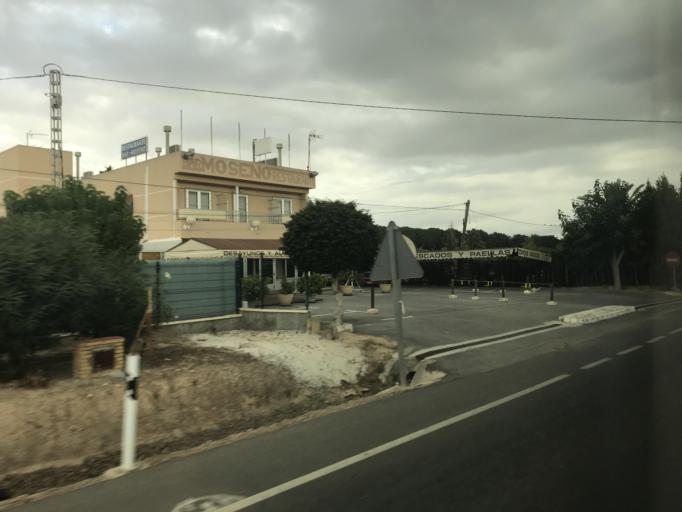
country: ES
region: Valencia
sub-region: Provincia de Alicante
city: Guardamar del Segura
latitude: 38.1252
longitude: -0.6518
